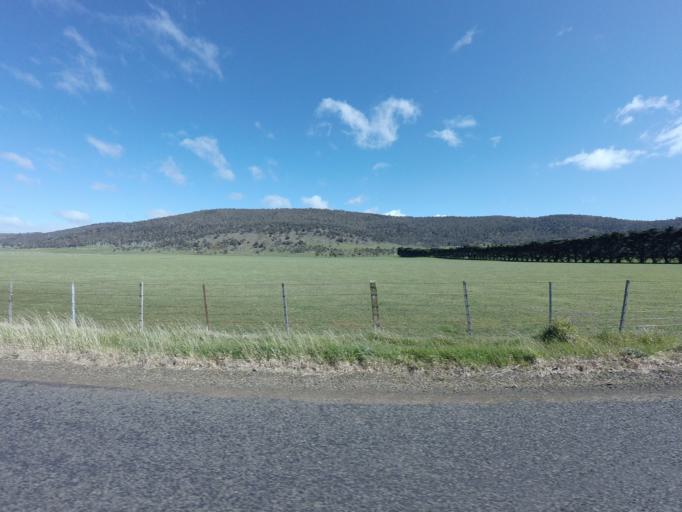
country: AU
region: Tasmania
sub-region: Northern Midlands
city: Evandale
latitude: -41.9671
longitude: 147.4414
